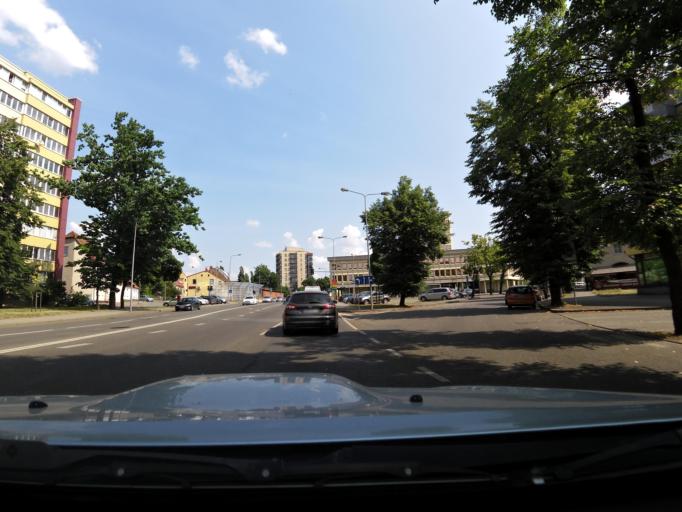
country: LT
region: Klaipedos apskritis
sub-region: Klaipeda
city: Klaipeda
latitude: 55.7187
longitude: 21.1187
